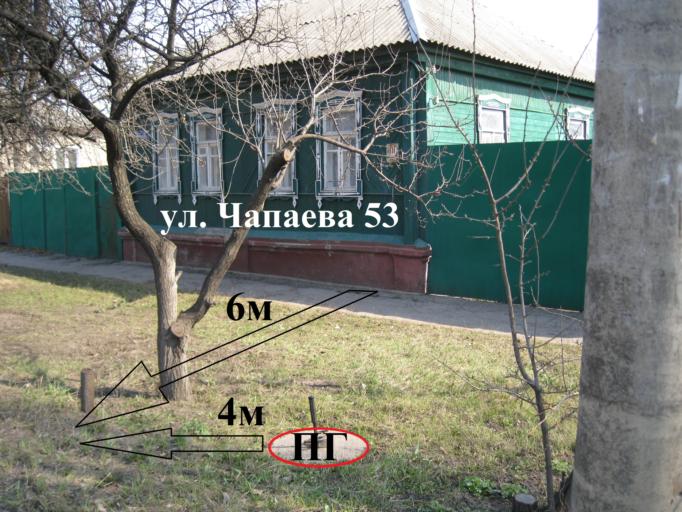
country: RU
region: Voronezj
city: Voronezh
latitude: 51.6395
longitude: 39.1871
